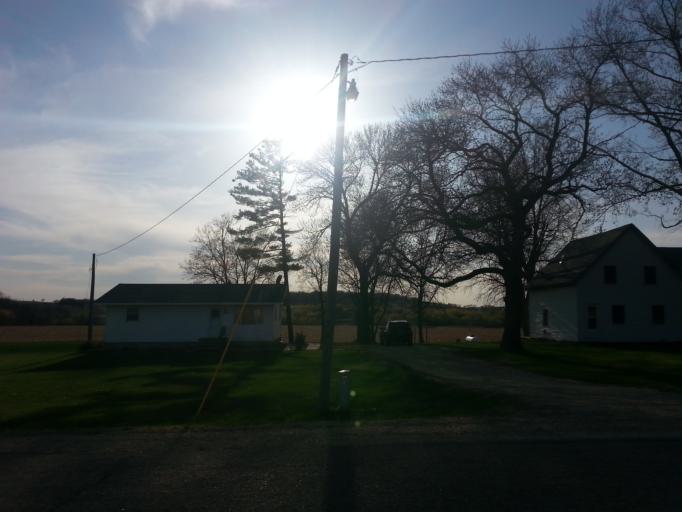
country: US
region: Wisconsin
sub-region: Pierce County
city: River Falls
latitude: 44.8053
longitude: -92.6448
